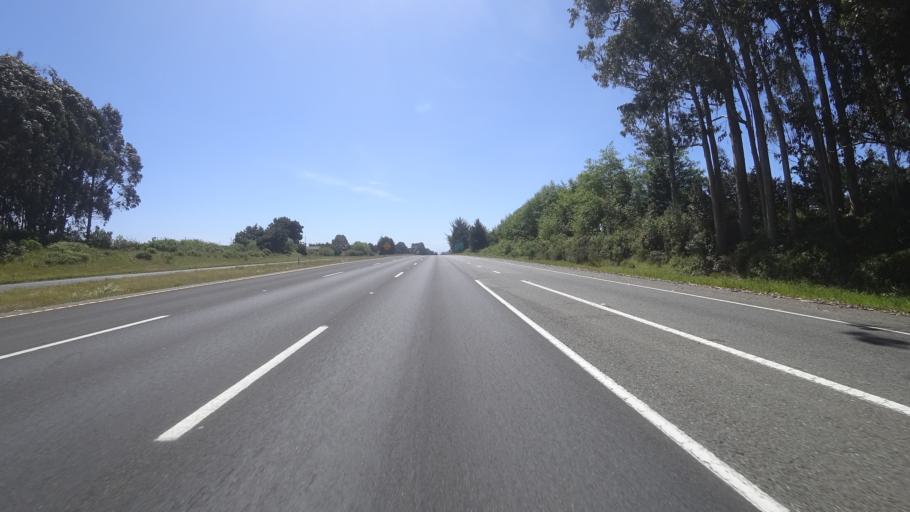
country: US
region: California
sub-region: Humboldt County
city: McKinleyville
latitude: 40.9740
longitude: -124.1169
